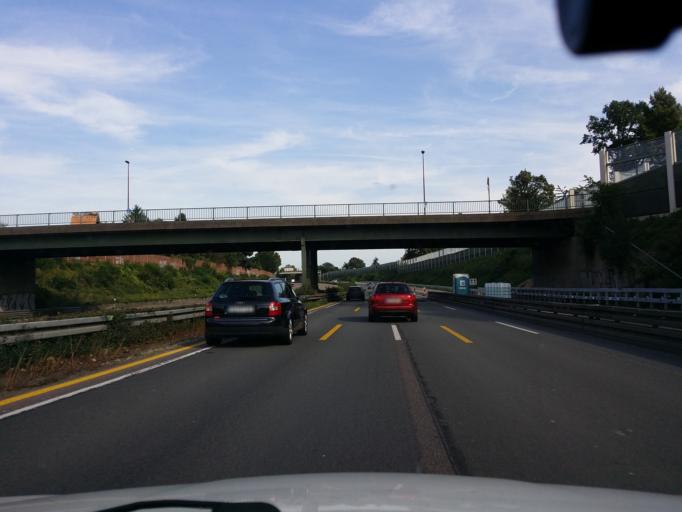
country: DE
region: North Rhine-Westphalia
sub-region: Regierungsbezirk Koln
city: Rath
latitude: 50.9199
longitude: 7.0726
